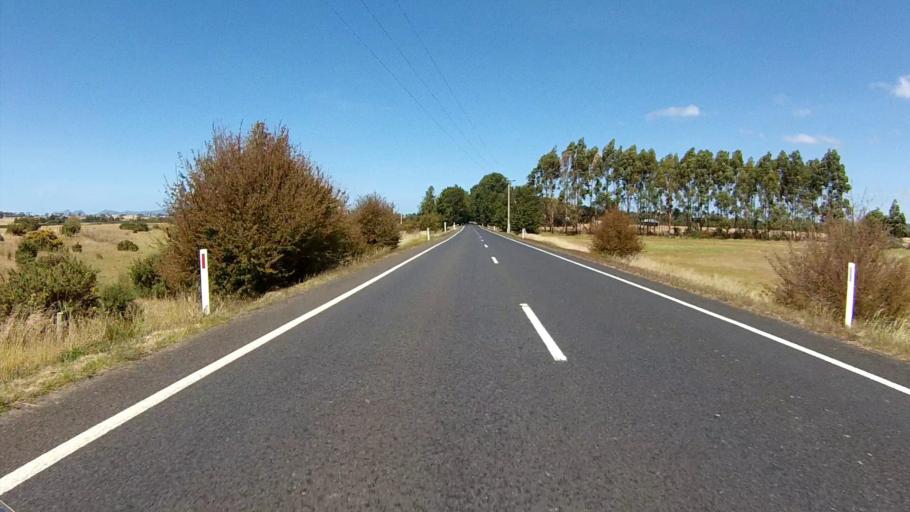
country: AU
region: Tasmania
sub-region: Break O'Day
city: St Helens
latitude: -42.0598
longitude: 148.0612
